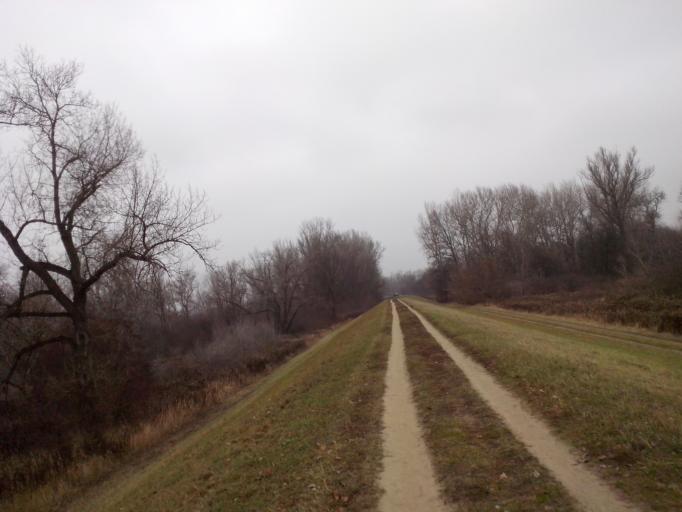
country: PL
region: Masovian Voivodeship
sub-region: Powiat legionowski
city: Jablonna
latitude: 52.3582
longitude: 20.9199
